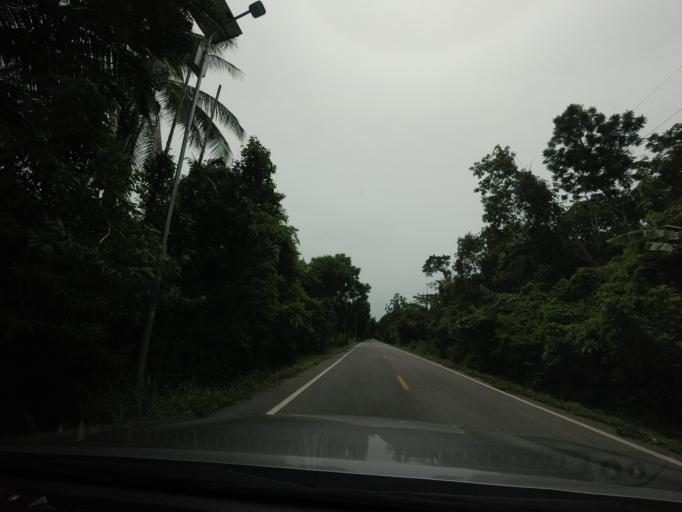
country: TH
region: Pattani
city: Kapho
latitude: 6.6017
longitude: 101.5323
